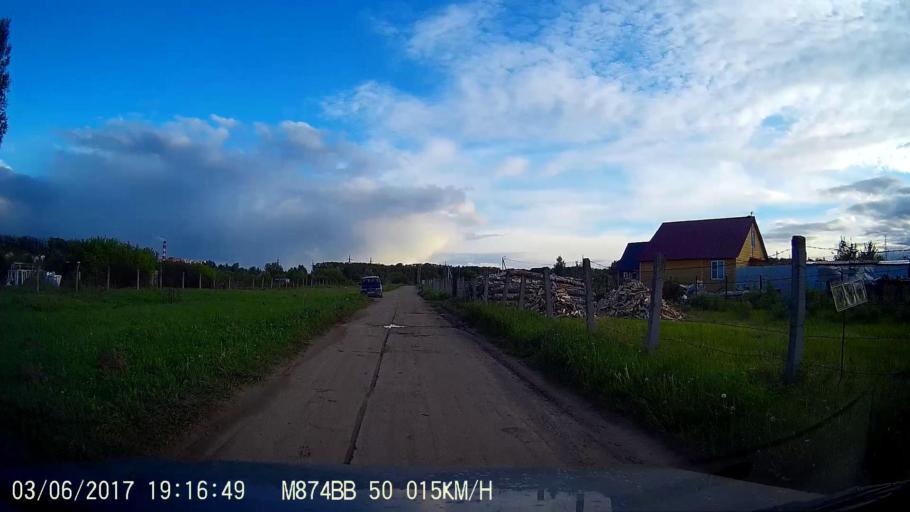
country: RU
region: Moskovskaya
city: Sychevo
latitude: 55.0711
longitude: 38.7382
